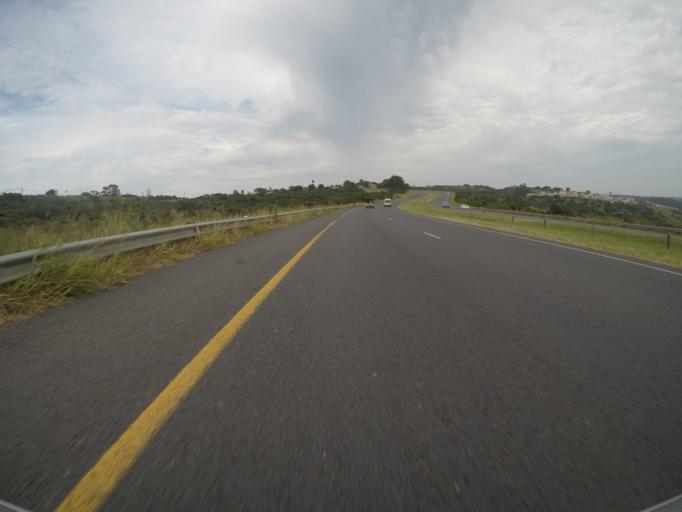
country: ZA
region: Eastern Cape
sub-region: Buffalo City Metropolitan Municipality
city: East London
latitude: -32.9703
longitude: 27.8824
